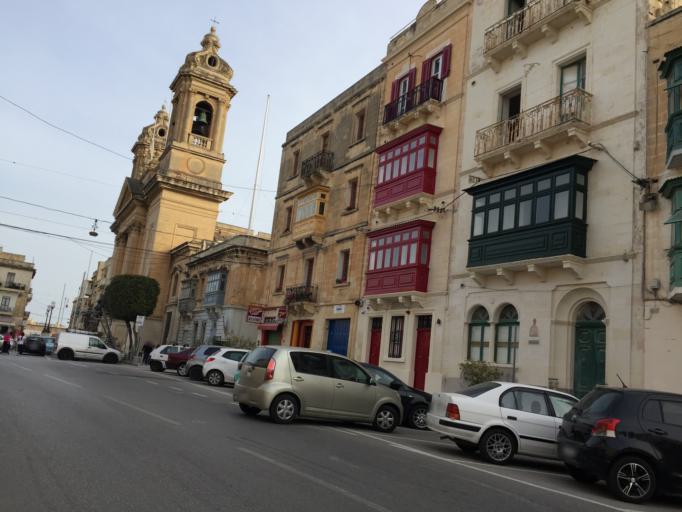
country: MT
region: L-Isla
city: Senglea
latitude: 35.8864
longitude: 14.5179
